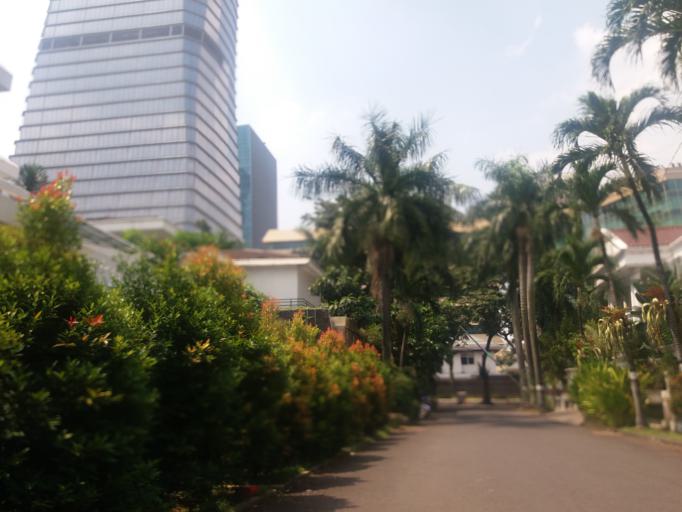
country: ID
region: Jakarta Raya
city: Jakarta
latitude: -6.2279
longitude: 106.8314
